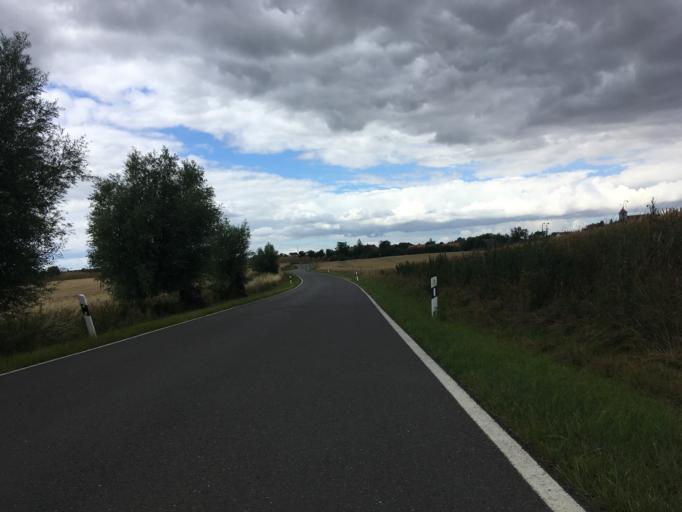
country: DE
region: Brandenburg
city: Gramzow
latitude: 53.2391
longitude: 13.9398
